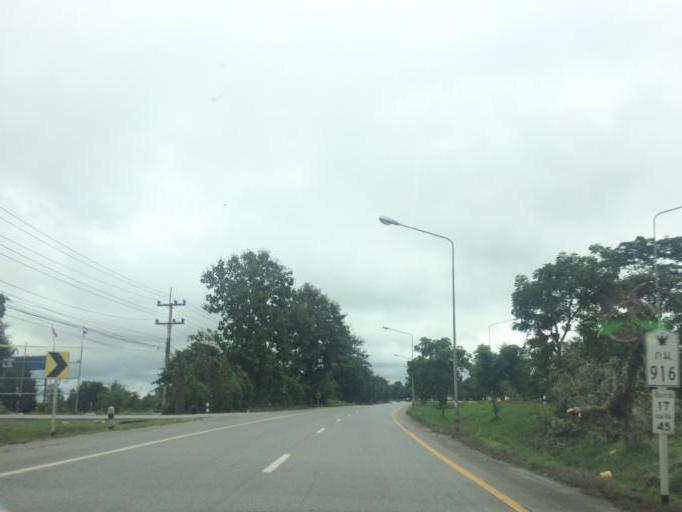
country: TH
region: Chiang Rai
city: Mae Lao
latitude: 19.7941
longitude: 99.7492
